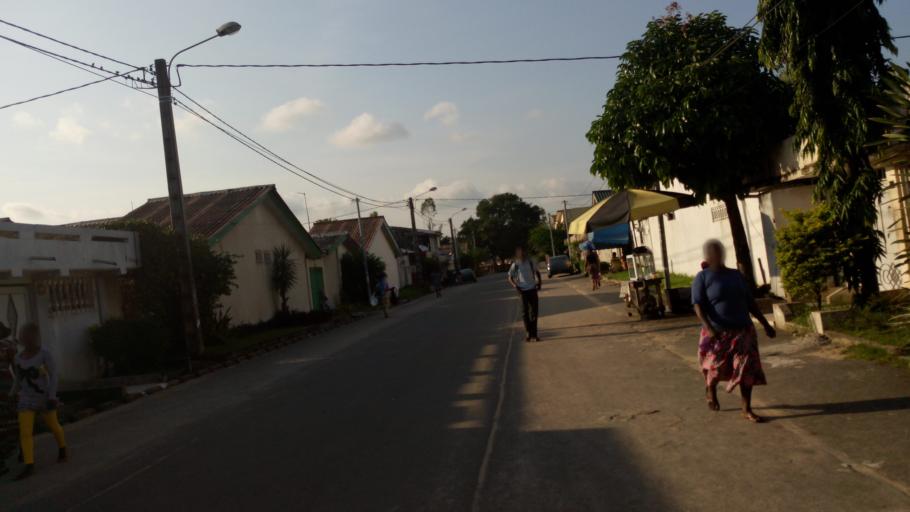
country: CI
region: Lagunes
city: Abobo
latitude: 5.4039
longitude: -3.9806
